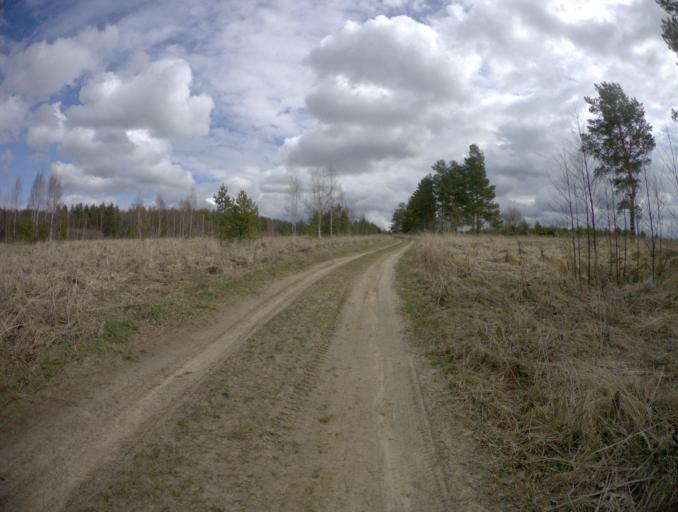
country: RU
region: Vladimir
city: Orgtrud
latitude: 56.0707
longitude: 40.6880
